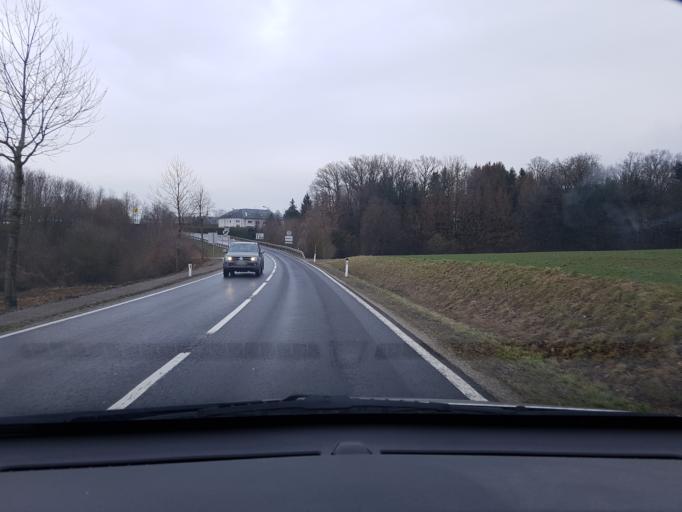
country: AT
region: Upper Austria
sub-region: Steyr Stadt
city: Steyr
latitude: 48.0802
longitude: 14.3718
